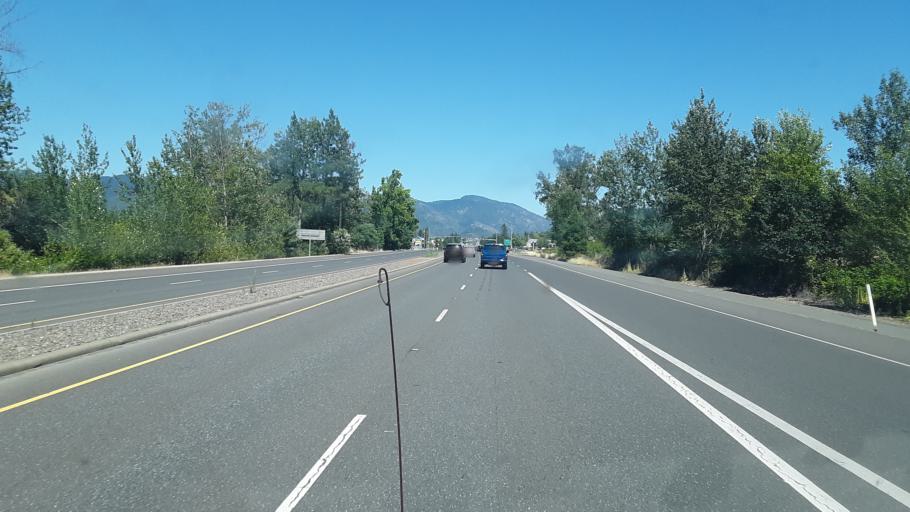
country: US
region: Oregon
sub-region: Josephine County
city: Redwood
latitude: 42.4176
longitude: -123.3719
